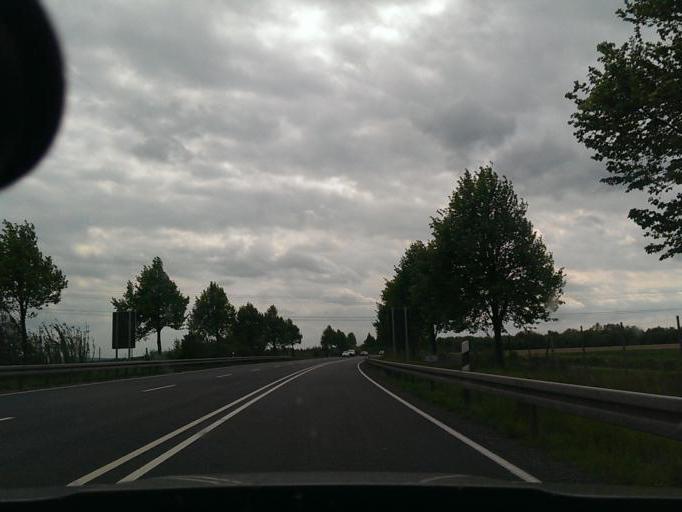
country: DE
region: Lower Saxony
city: Pattensen
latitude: 52.2546
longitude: 9.7830
